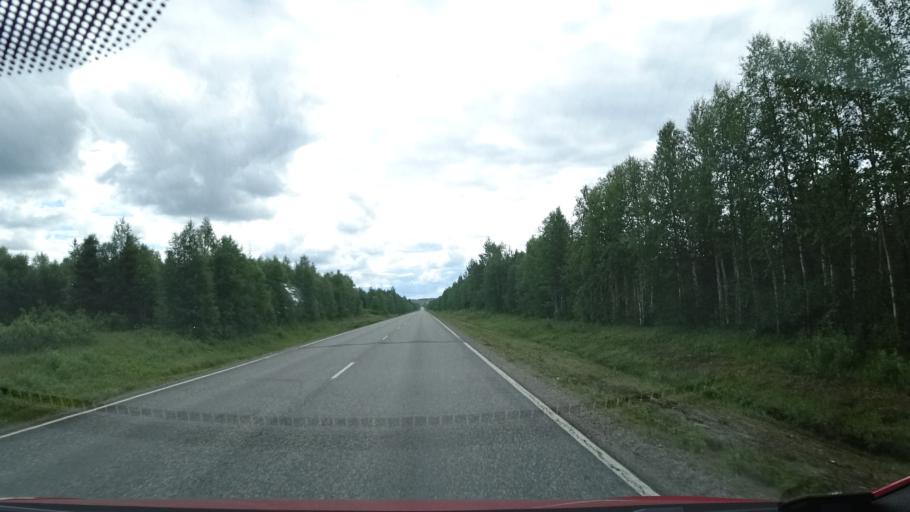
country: FI
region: Lapland
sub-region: Tunturi-Lappi
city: Kittilae
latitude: 67.5856
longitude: 24.9246
